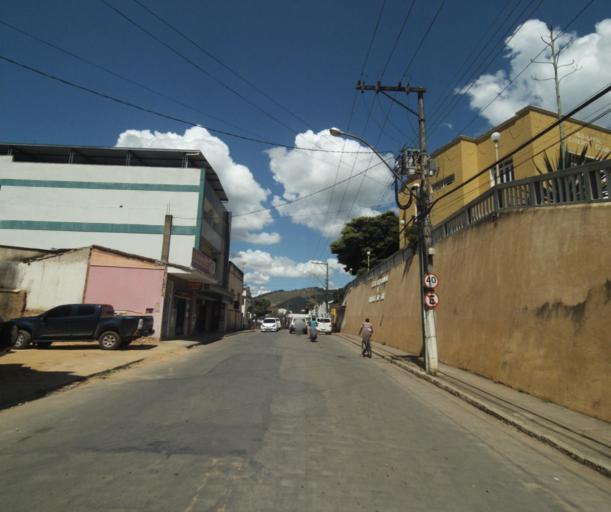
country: BR
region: Espirito Santo
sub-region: Mimoso Do Sul
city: Mimoso do Sul
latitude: -21.0638
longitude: -41.3626
